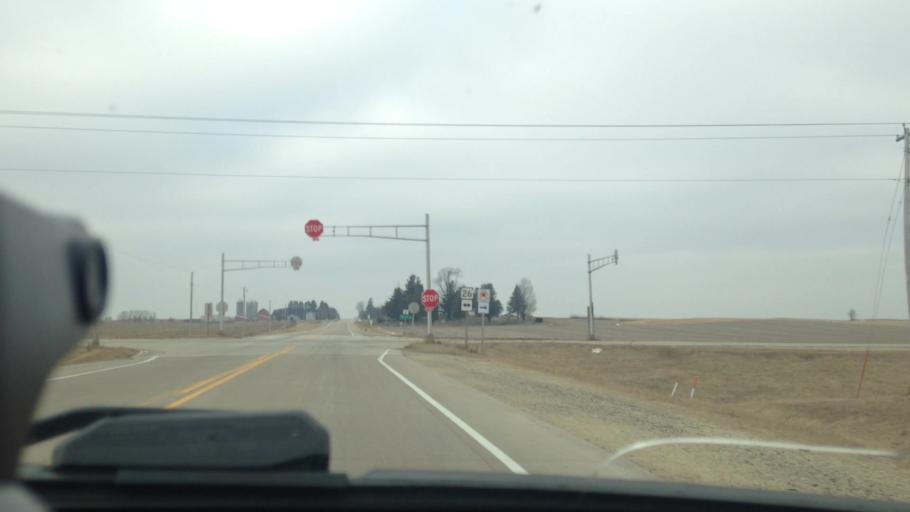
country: US
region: Wisconsin
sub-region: Dodge County
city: Juneau
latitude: 43.4735
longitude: -88.7030
